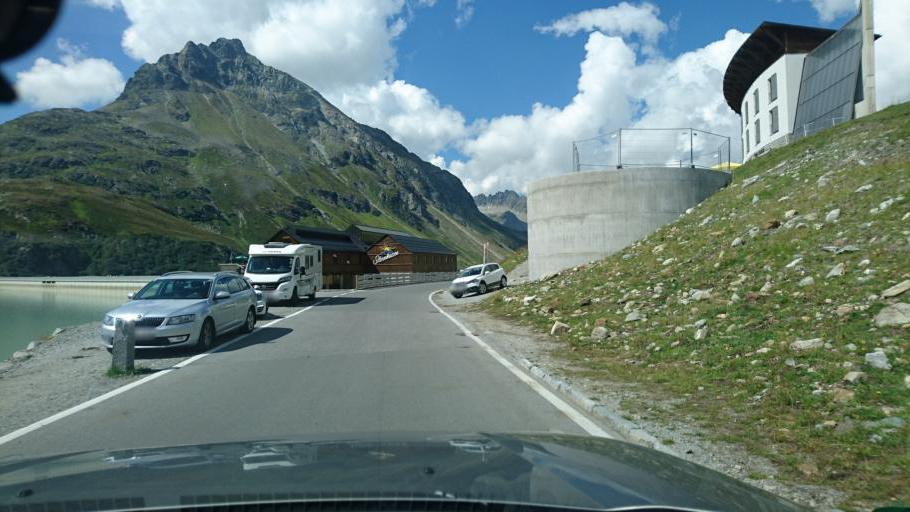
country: AT
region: Vorarlberg
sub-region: Politischer Bezirk Bludenz
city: Gaschurn
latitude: 46.9177
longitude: 10.0943
